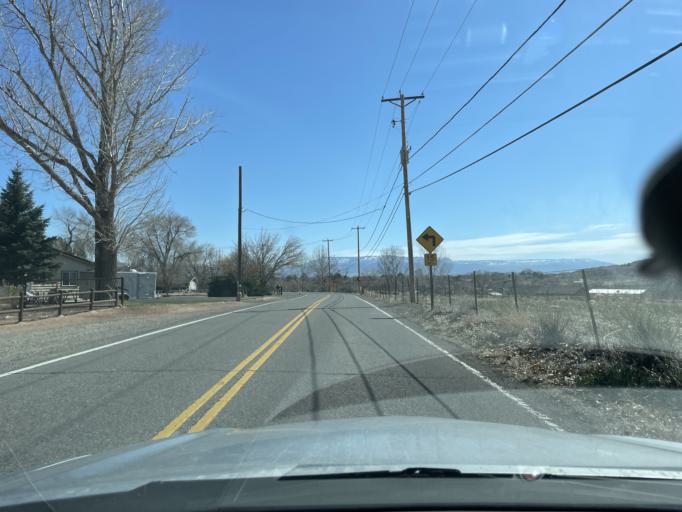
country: US
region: Colorado
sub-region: Mesa County
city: Redlands
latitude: 39.0885
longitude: -108.6652
